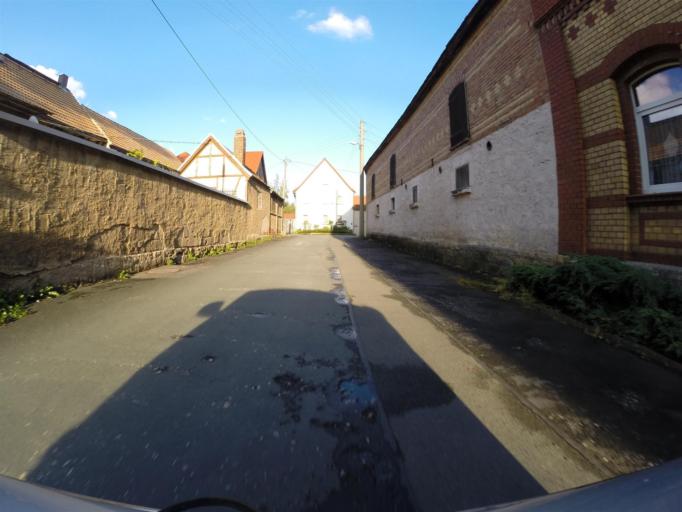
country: DE
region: Thuringia
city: Bucha
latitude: 50.8799
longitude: 11.5124
